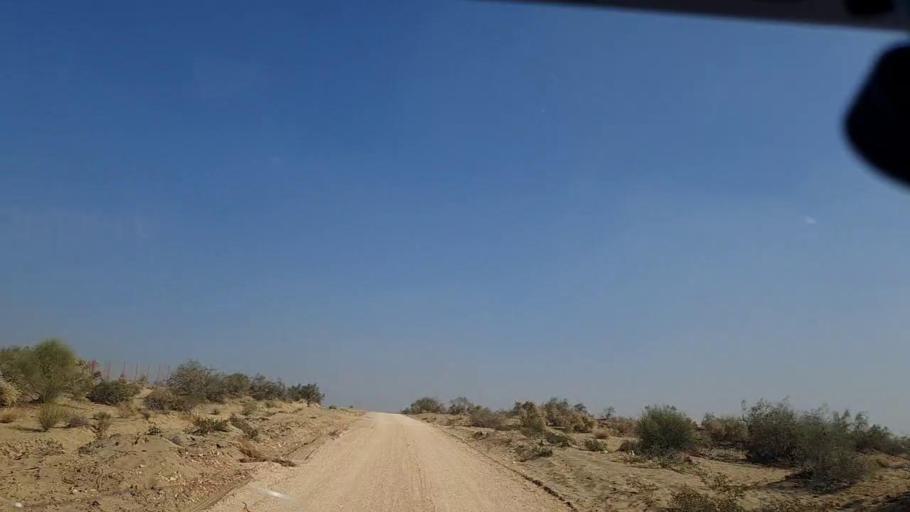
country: PK
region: Sindh
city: Khanpur
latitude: 27.5575
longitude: 69.3898
